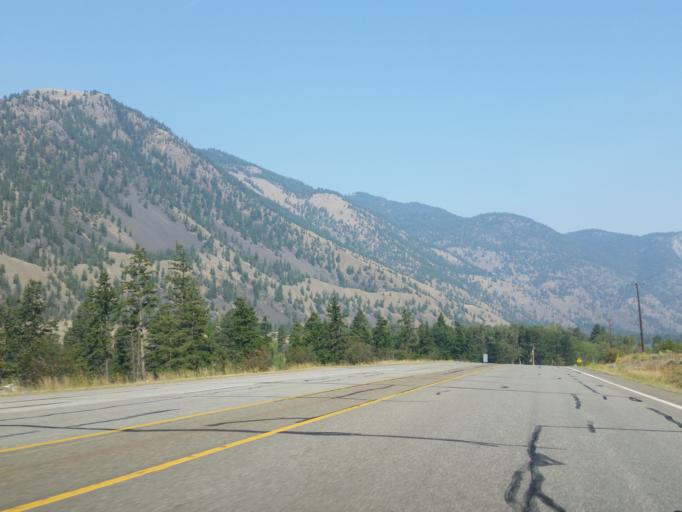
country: CA
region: British Columbia
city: Oliver
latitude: 49.2522
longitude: -120.0109
